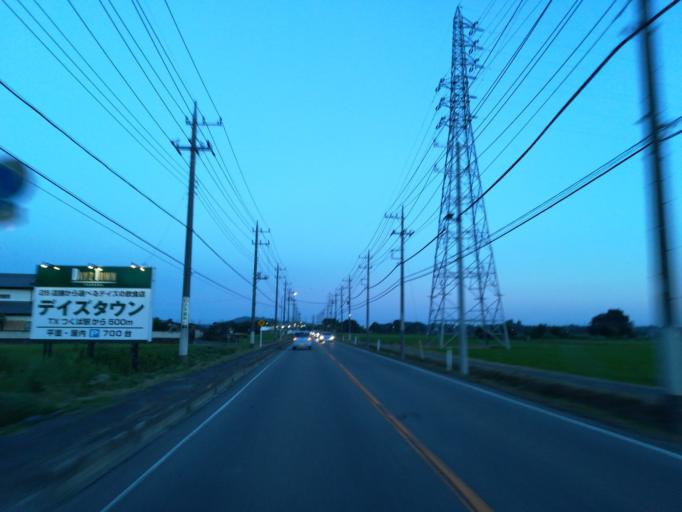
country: JP
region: Ibaraki
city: Tsukuba
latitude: 36.2196
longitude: 140.0653
